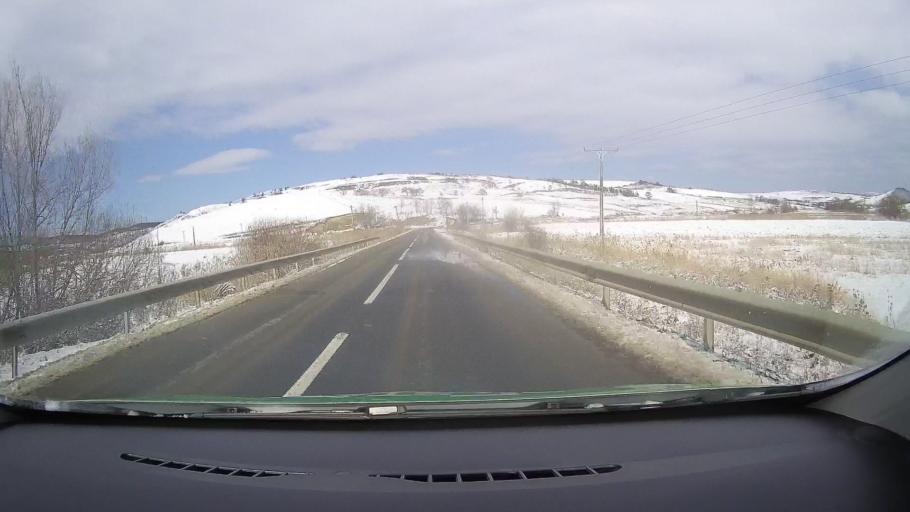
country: RO
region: Sibiu
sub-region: Comuna Altina
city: Altina
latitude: 45.9765
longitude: 24.4657
